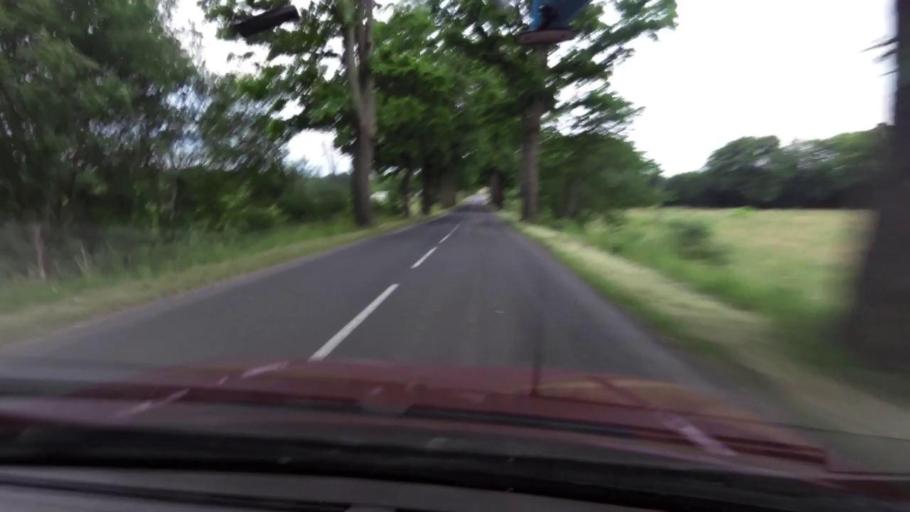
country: PL
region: West Pomeranian Voivodeship
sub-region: Powiat koszalinski
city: Sianow
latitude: 54.1764
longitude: 16.3879
